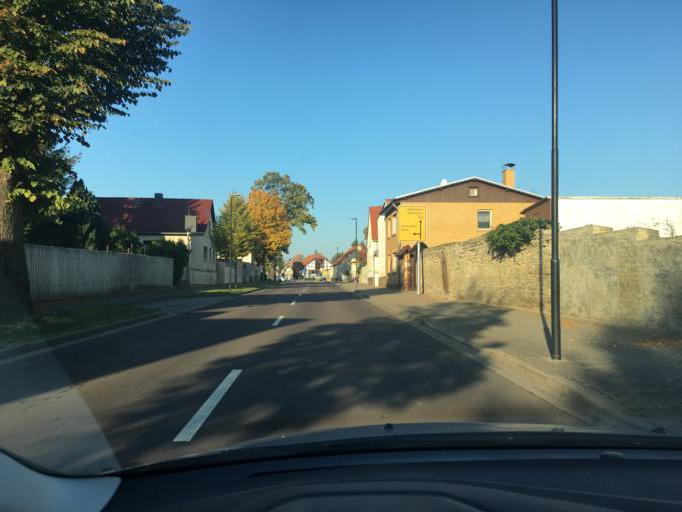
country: DE
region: Saxony-Anhalt
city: Welsleben
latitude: 52.0009
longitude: 11.6403
